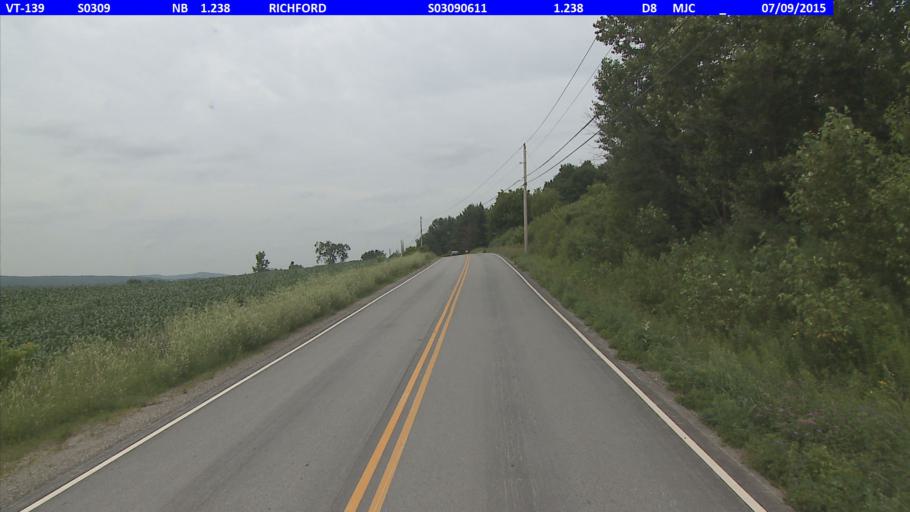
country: US
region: Vermont
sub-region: Franklin County
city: Richford
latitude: 45.0061
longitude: -72.6606
